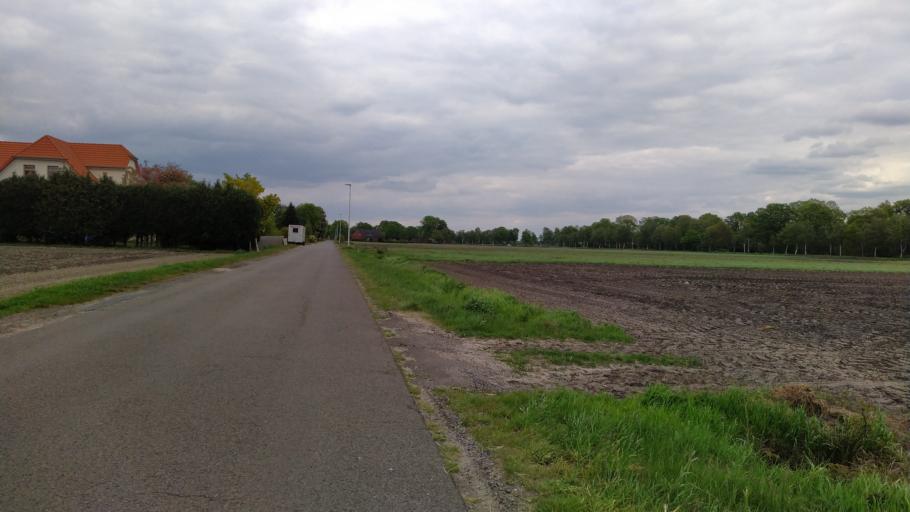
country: DE
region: Lower Saxony
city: Grasberg
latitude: 53.1827
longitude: 9.0081
